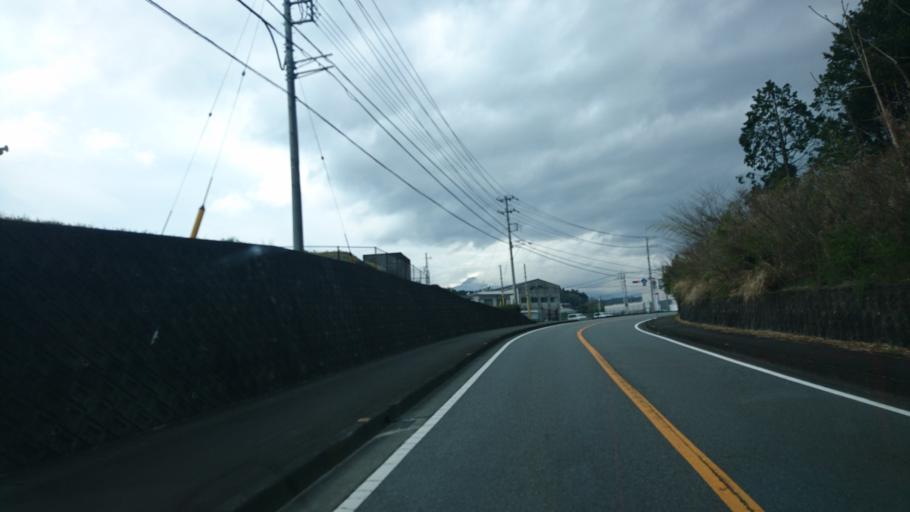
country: JP
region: Shizuoka
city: Fujinomiya
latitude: 35.2654
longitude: 138.6037
